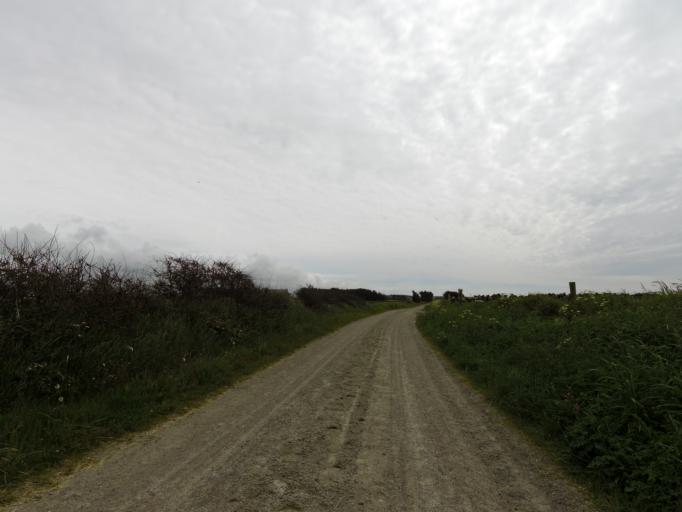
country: NO
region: Rogaland
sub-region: Ha
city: Naerbo
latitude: 58.6751
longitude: 5.5480
